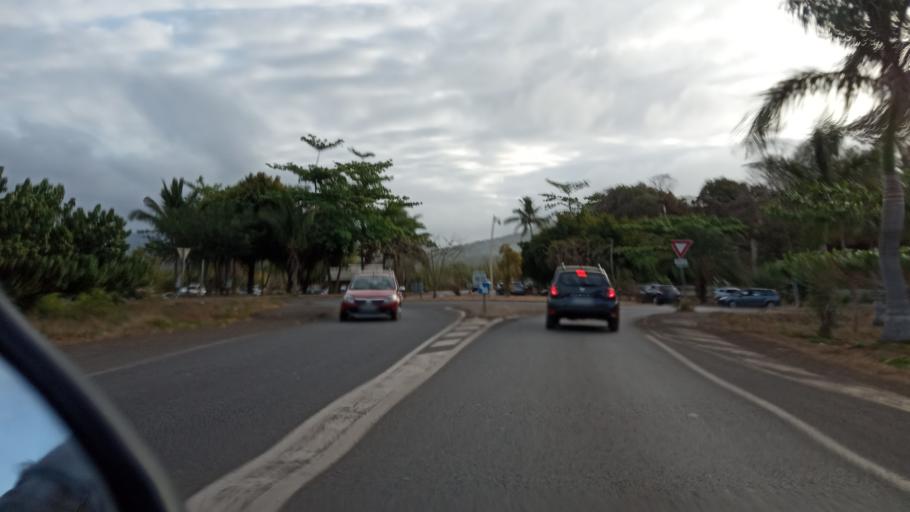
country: YT
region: Mamoudzou
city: Mamoudzou
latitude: -12.8043
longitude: 45.2113
